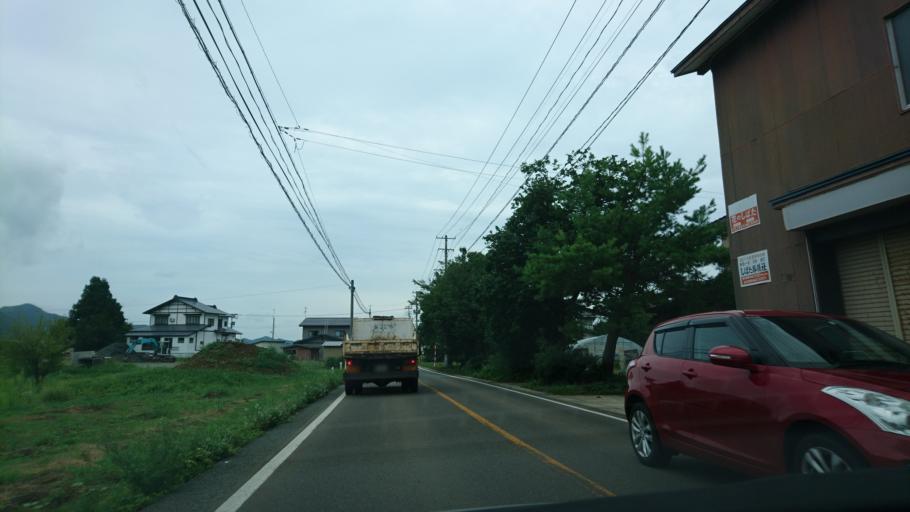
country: JP
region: Akita
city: Yuzawa
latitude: 39.1163
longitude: 140.5822
